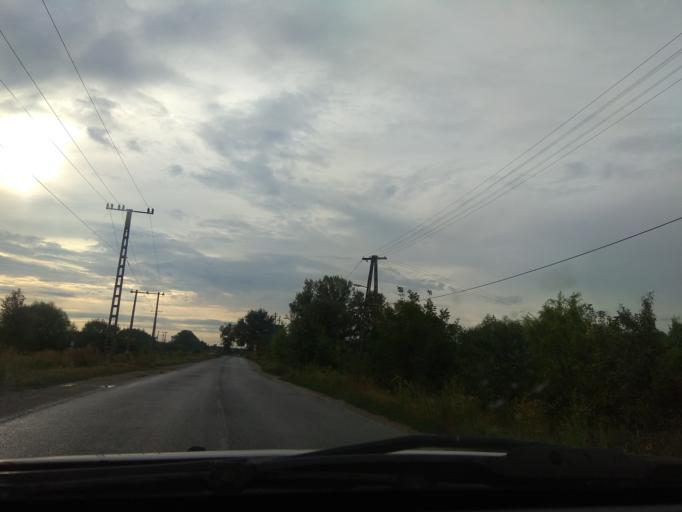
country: HU
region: Borsod-Abauj-Zemplen
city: Gesztely
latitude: 48.1084
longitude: 20.9586
